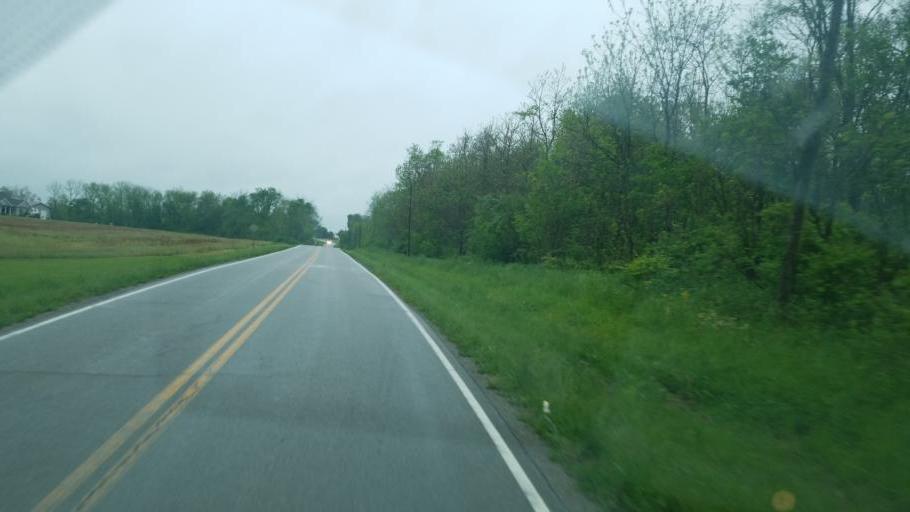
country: US
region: Ohio
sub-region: Highland County
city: Leesburg
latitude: 39.3009
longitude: -83.5790
